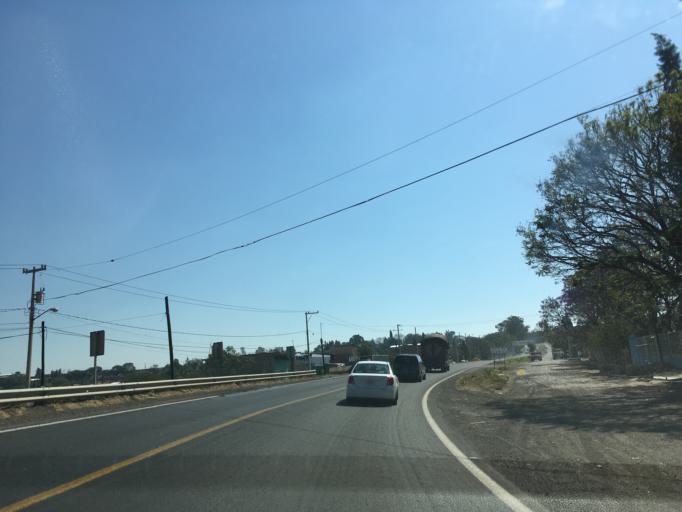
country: MX
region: Michoacan
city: Indaparapeo
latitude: 19.7883
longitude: -100.9799
